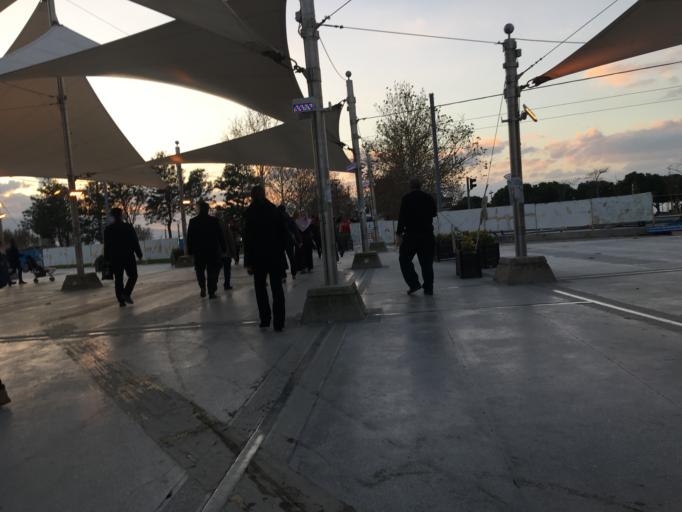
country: TR
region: Izmir
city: Izmir
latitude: 38.4186
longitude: 27.1275
